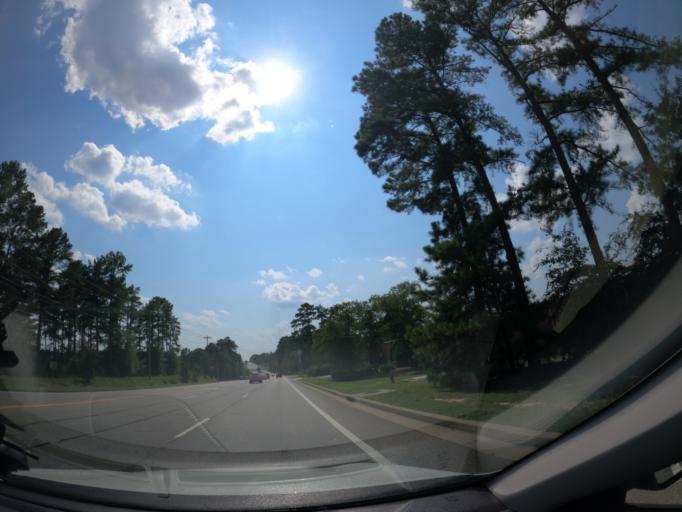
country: US
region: South Carolina
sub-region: Lexington County
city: Springdale
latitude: 33.9536
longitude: -81.1250
